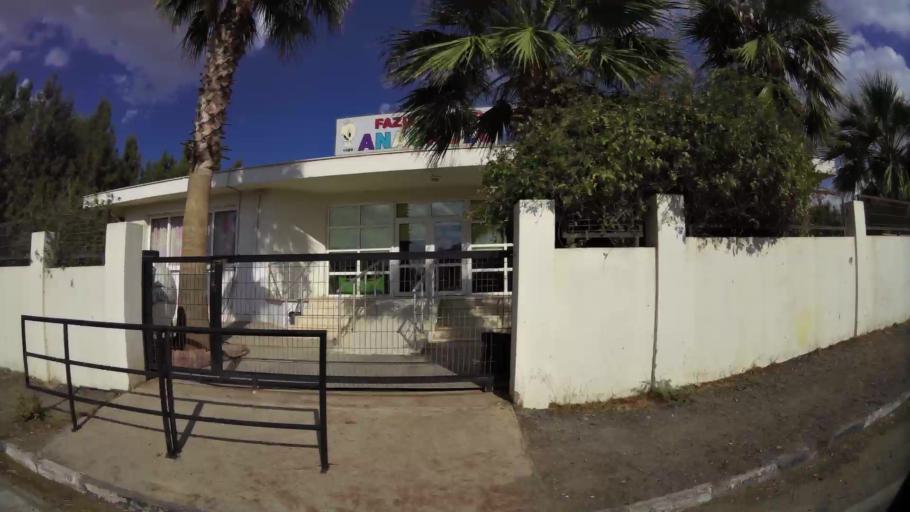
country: CY
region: Lefkosia
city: Nicosia
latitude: 35.1944
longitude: 33.3491
